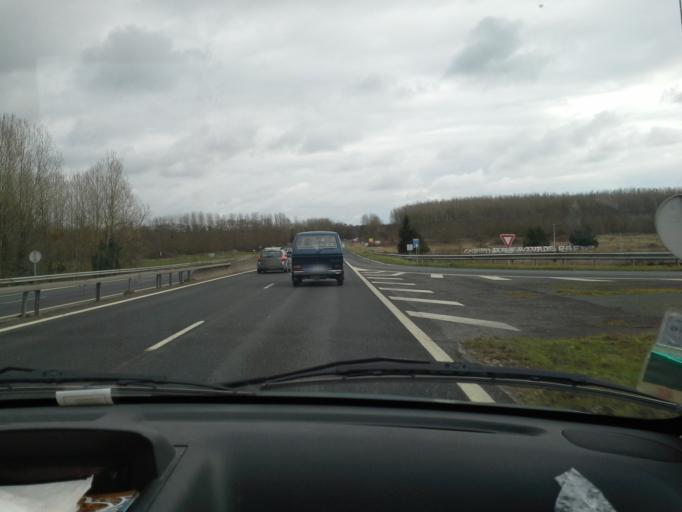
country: FR
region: Centre
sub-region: Departement du Loir-et-Cher
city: Vineuil
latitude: 47.5902
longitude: 1.3589
